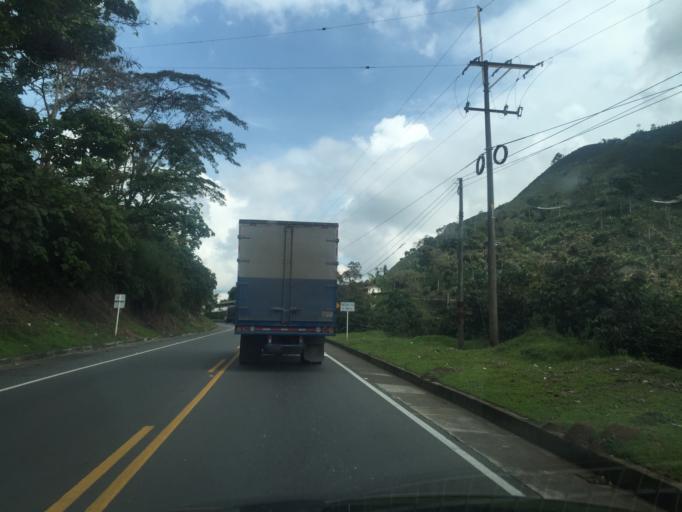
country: CO
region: Caldas
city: Chinchina
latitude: 4.9970
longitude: -75.5725
